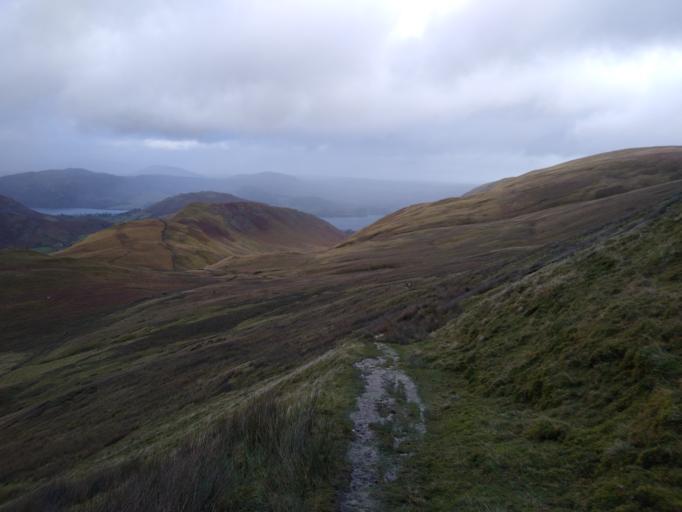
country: GB
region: England
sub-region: Cumbria
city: Ambleside
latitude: 54.5385
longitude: -2.8523
